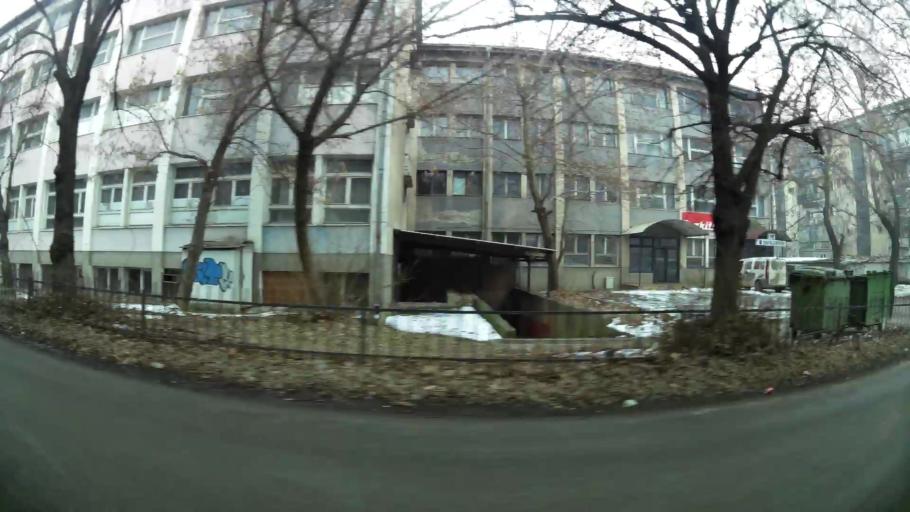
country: MK
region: Cair
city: Cair
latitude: 42.0060
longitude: 21.4654
